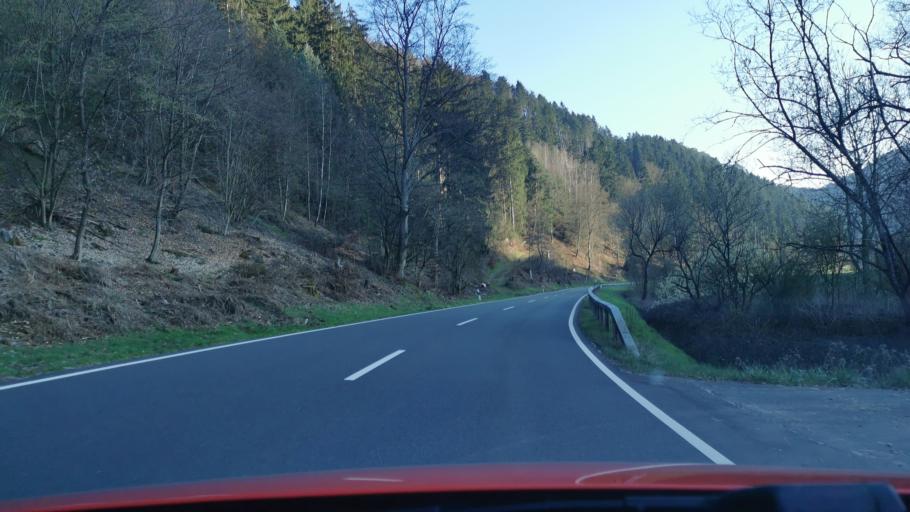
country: DE
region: Rheinland-Pfalz
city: Kordel
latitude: 49.8297
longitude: 6.6536
